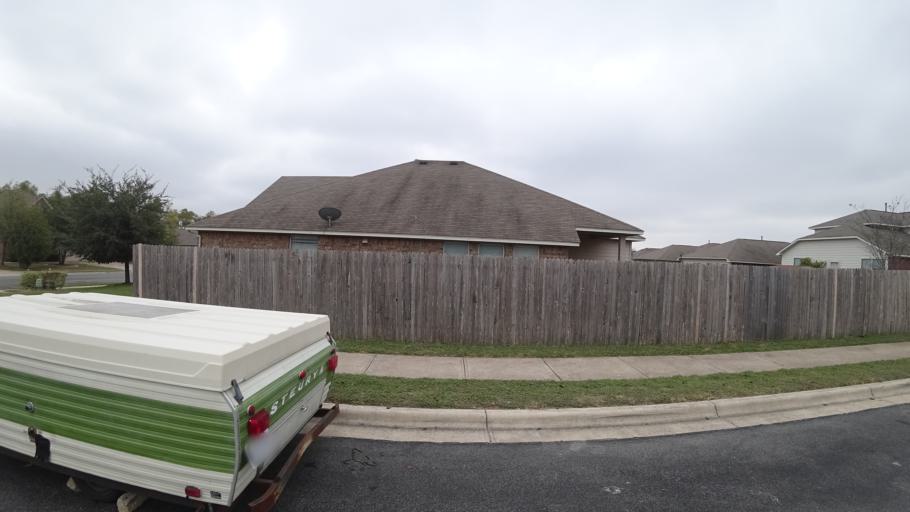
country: US
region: Texas
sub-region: Travis County
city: Pflugerville
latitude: 30.3778
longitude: -97.6535
